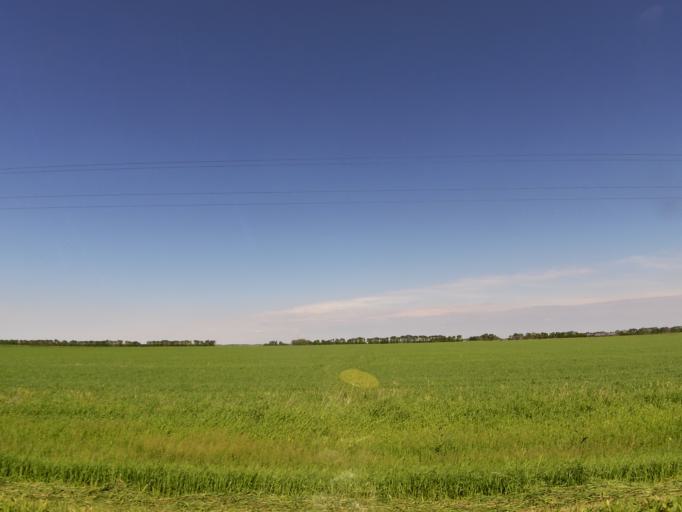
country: US
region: North Dakota
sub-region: Walsh County
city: Grafton
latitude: 48.3225
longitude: -97.2553
